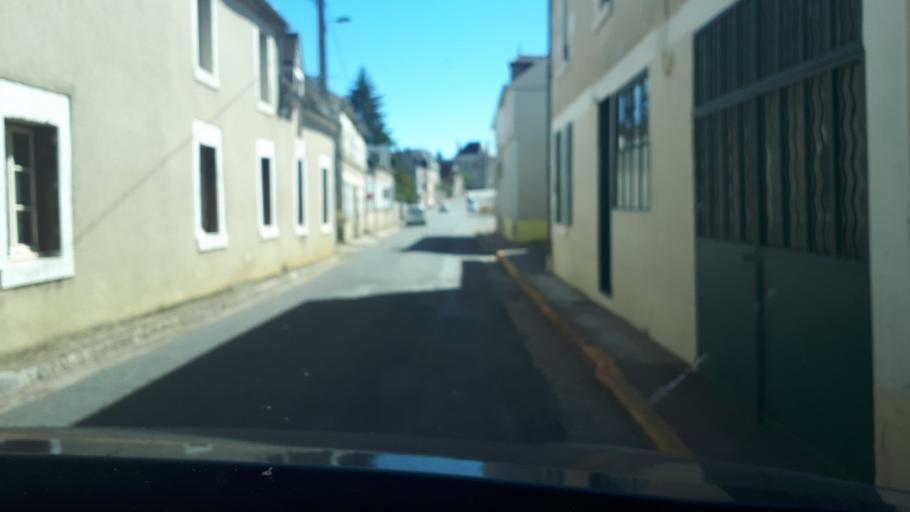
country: FR
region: Centre
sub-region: Departement du Cher
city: Sancerre
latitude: 47.2586
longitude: 2.7561
